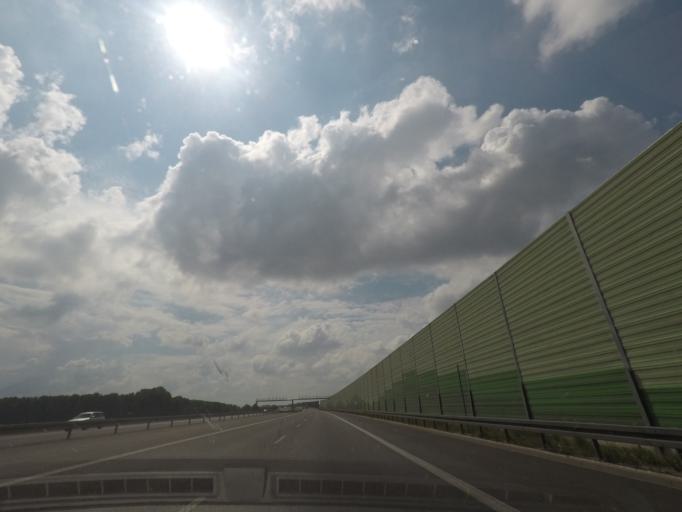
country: PL
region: Lodz Voivodeship
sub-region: Powiat kutnowski
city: Krzyzanow
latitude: 52.1444
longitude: 19.4822
